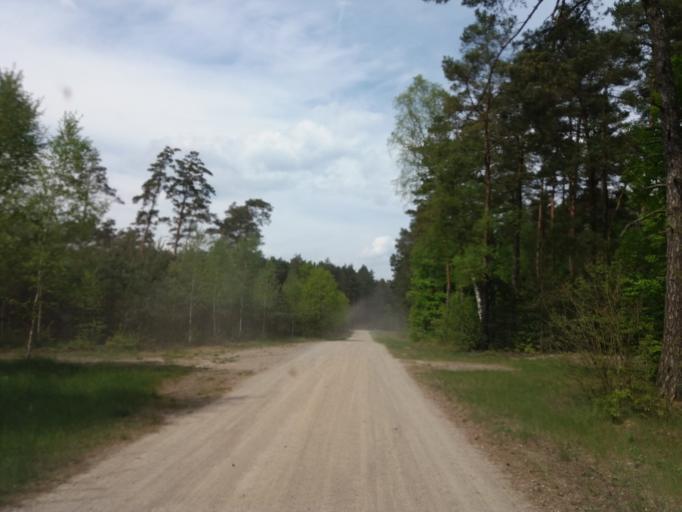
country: PL
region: West Pomeranian Voivodeship
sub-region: Powiat choszczenski
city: Drawno
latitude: 53.2031
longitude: 15.7170
